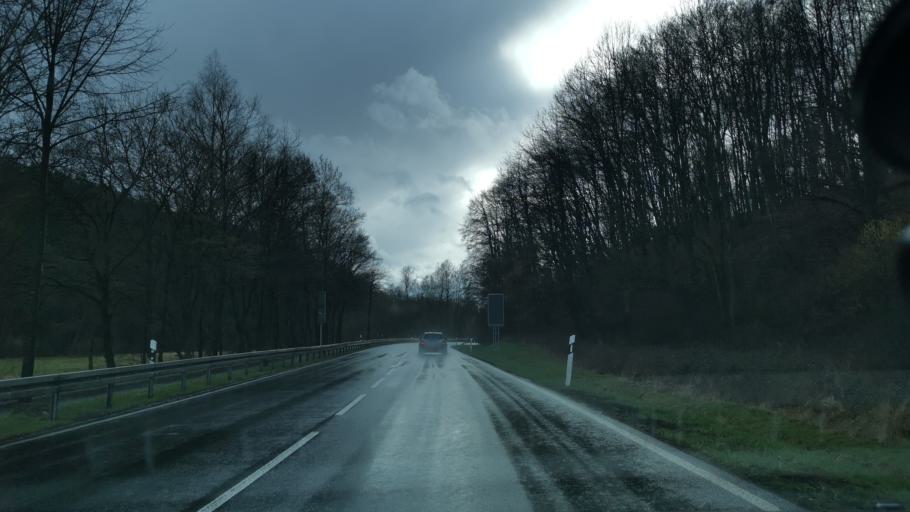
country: DE
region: Hesse
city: Bebra
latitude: 50.9936
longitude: 9.8094
